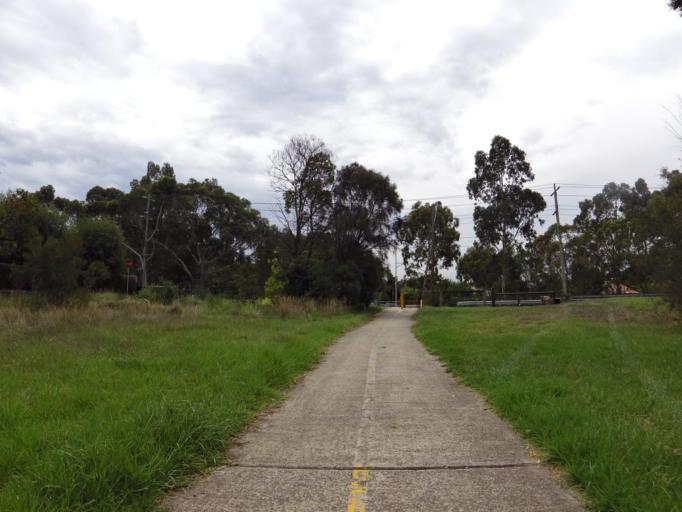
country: AU
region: Victoria
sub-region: Moonee Valley
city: Essendon West
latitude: -37.7483
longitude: 144.8811
